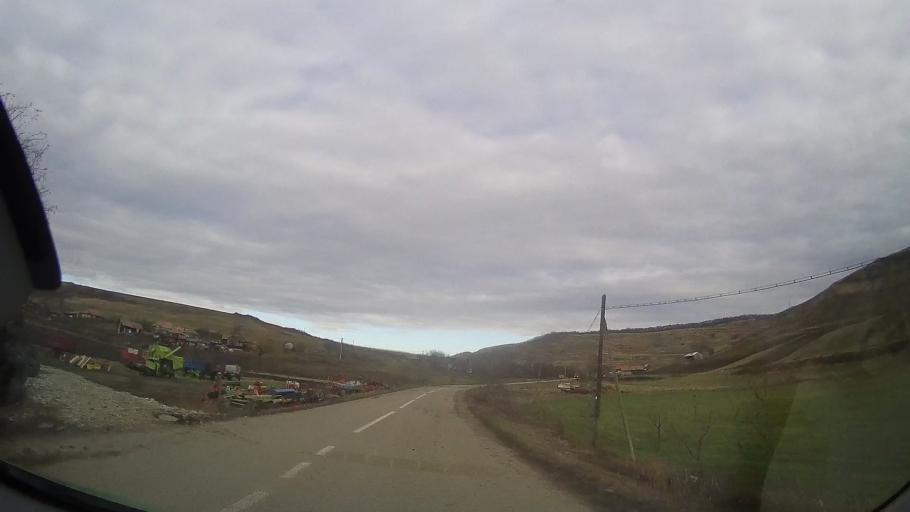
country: RO
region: Bistrita-Nasaud
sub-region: Comuna Micestii de Campie
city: Micestii de Campie
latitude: 46.8341
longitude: 24.3023
